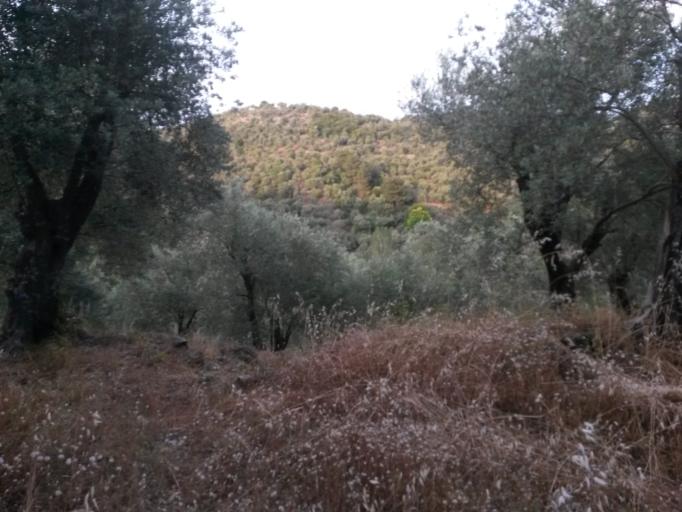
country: GR
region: North Aegean
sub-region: Nomos Lesvou
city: Agiasos
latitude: 39.0986
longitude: 26.3964
